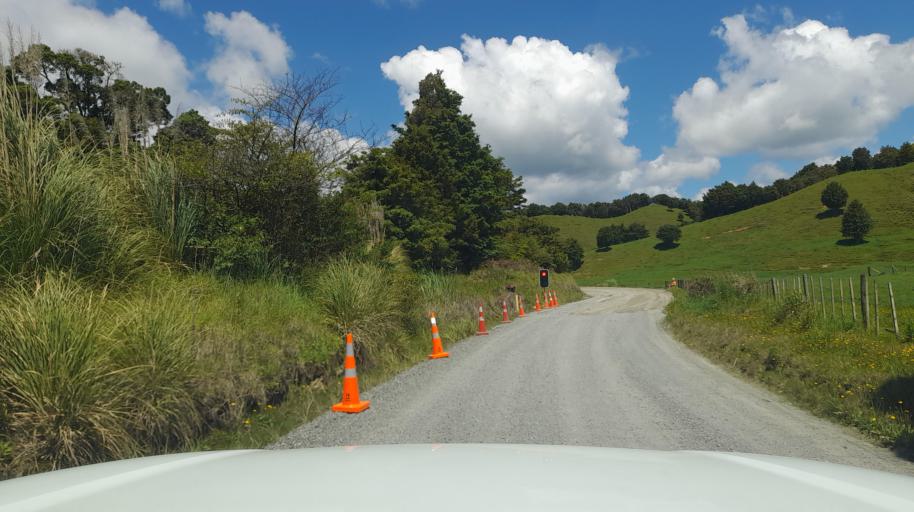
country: NZ
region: Northland
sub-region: Far North District
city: Kaitaia
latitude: -35.1070
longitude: 173.3921
